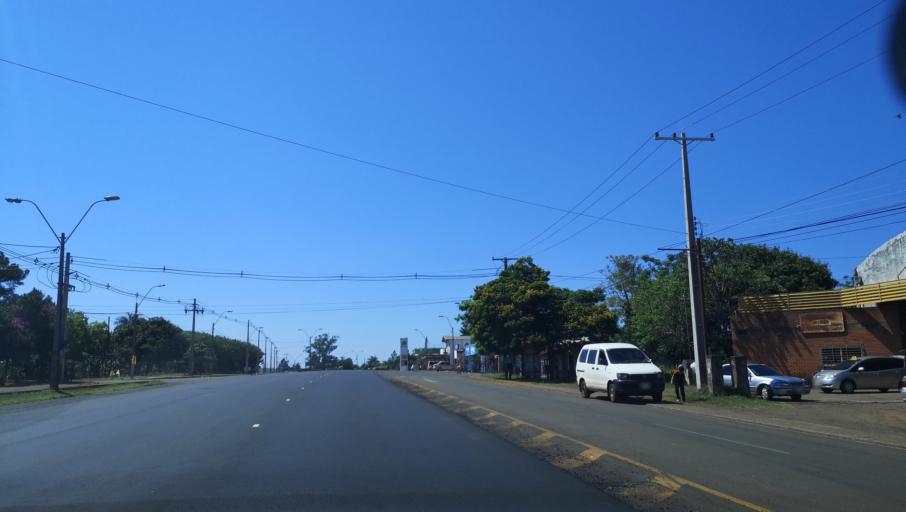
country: PY
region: Itapua
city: Carmen del Parana
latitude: -27.2178
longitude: -56.1460
